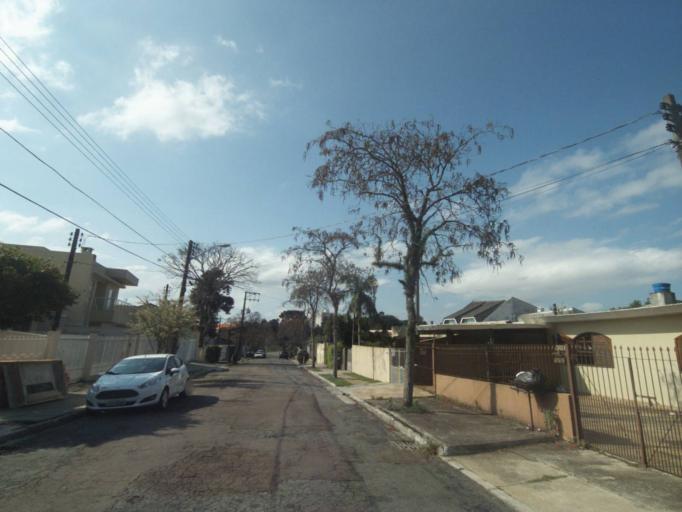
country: BR
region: Parana
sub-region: Pinhais
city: Pinhais
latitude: -25.4043
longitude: -49.2129
